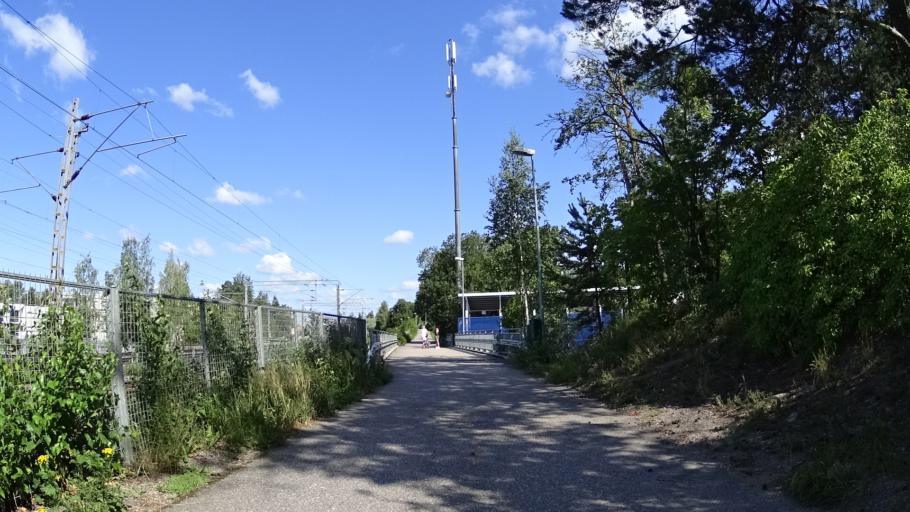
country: FI
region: Uusimaa
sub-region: Helsinki
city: Jaervenpaeae
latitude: 60.4644
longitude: 25.0999
